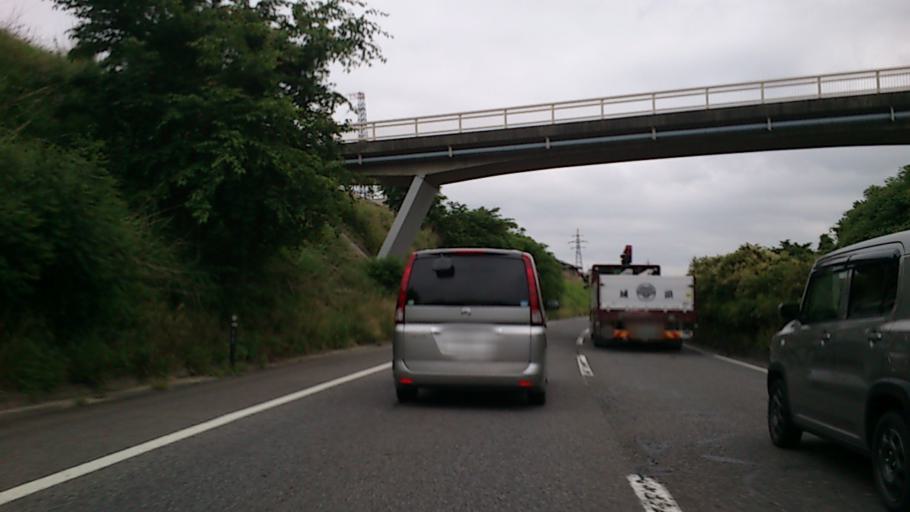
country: JP
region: Fukushima
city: Koriyama
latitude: 37.3783
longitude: 140.3479
